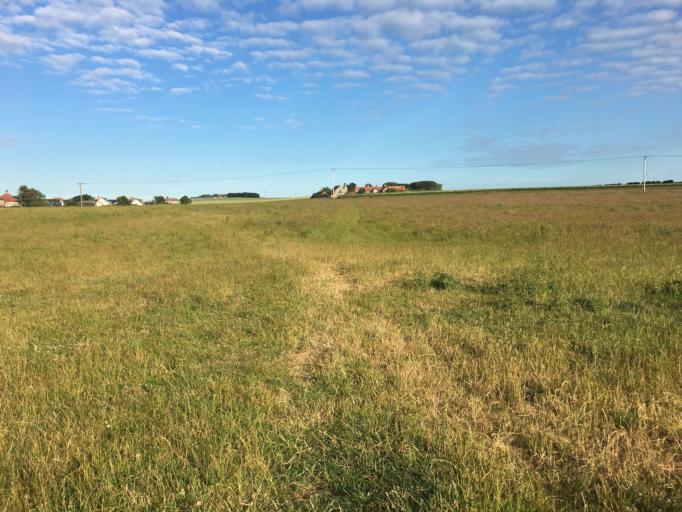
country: GB
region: England
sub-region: Northumberland
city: Bamburgh
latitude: 55.6051
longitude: -1.7052
